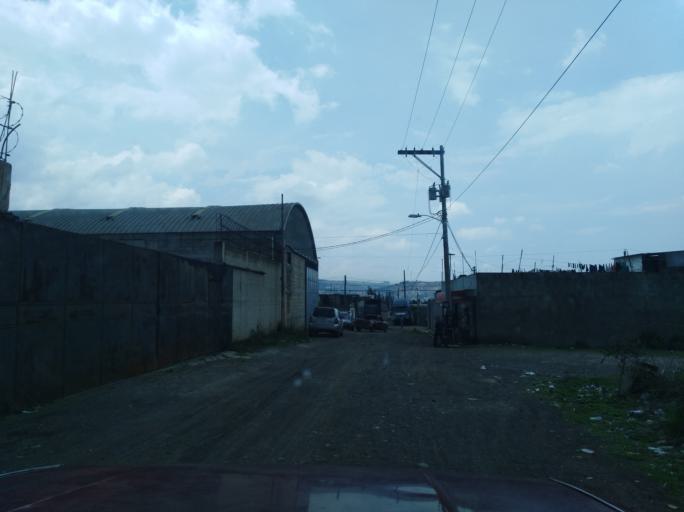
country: GT
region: Guatemala
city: Villa Nueva
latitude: 14.5247
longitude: -90.6232
